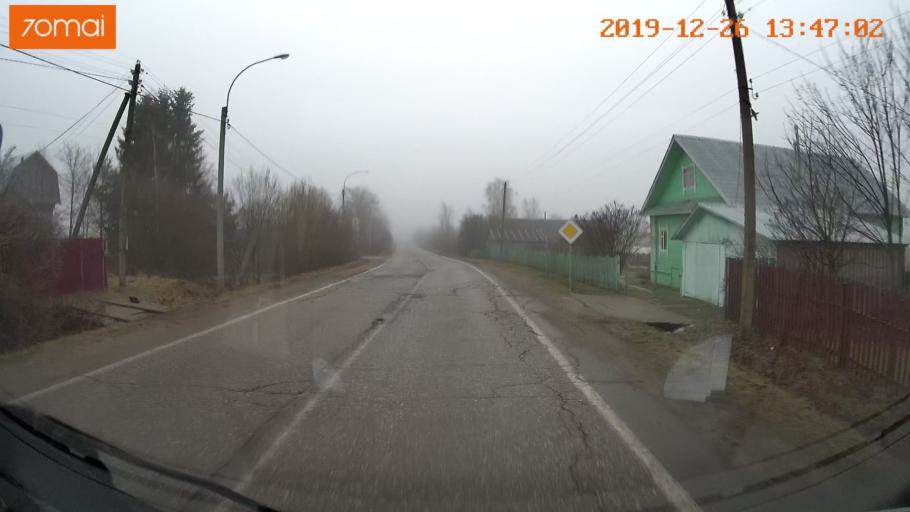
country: RU
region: Vologda
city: Sheksna
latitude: 58.6876
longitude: 38.5305
